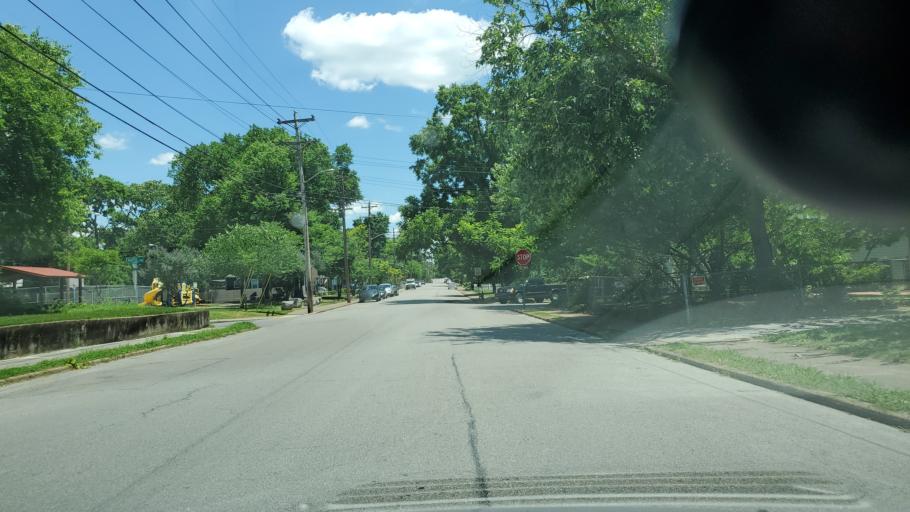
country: US
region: Tennessee
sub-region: Davidson County
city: Nashville
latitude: 36.1921
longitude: -86.7402
